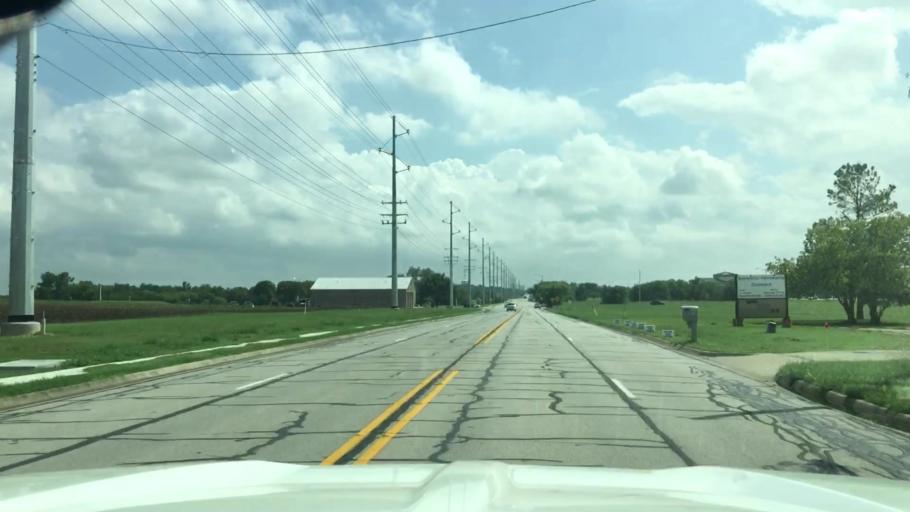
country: US
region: Texas
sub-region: Denton County
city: Denton
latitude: 33.2424
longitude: -97.1607
